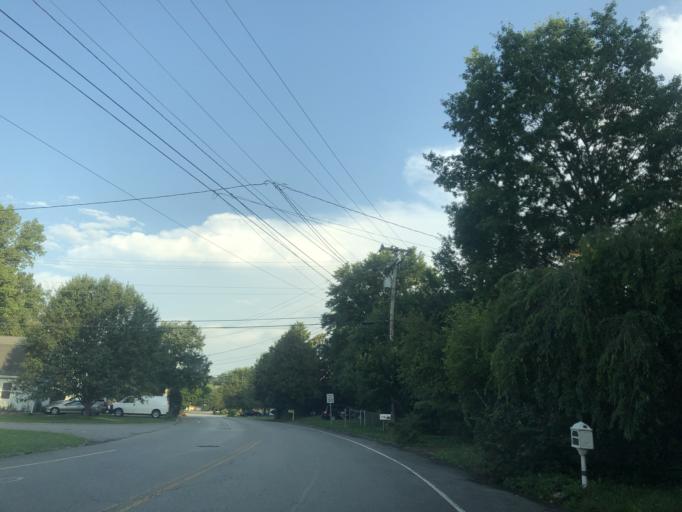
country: US
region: Tennessee
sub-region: Davidson County
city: Lakewood
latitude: 36.1355
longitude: -86.6404
